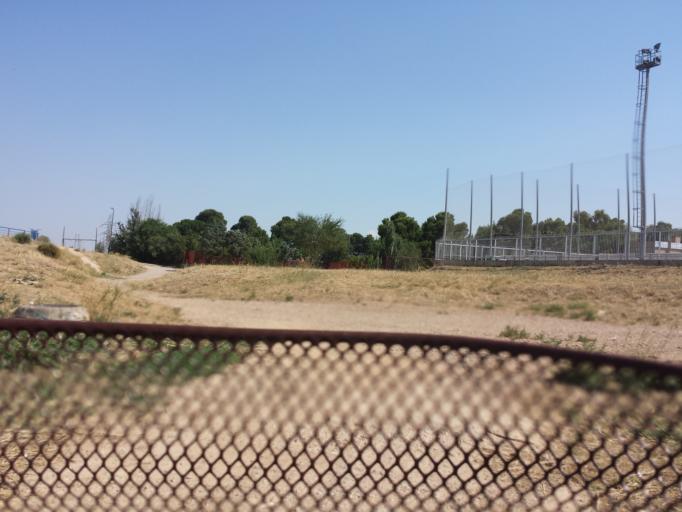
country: ES
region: Aragon
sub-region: Provincia de Zaragoza
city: Zaragoza
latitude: 41.6343
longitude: -0.8711
